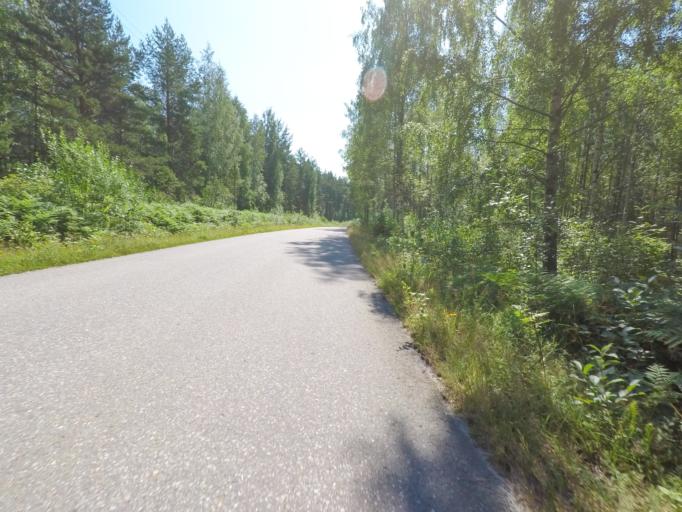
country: FI
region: Southern Savonia
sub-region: Mikkeli
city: Puumala
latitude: 61.4429
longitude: 28.1639
